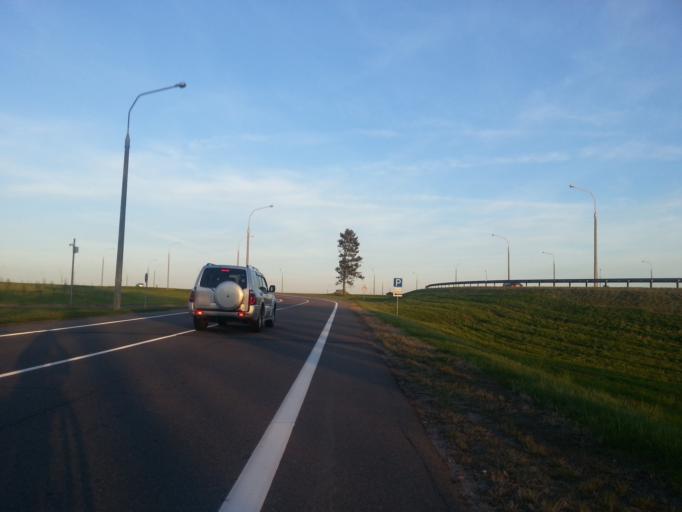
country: BY
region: Minsk
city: Slabada
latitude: 54.0180
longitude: 27.8922
